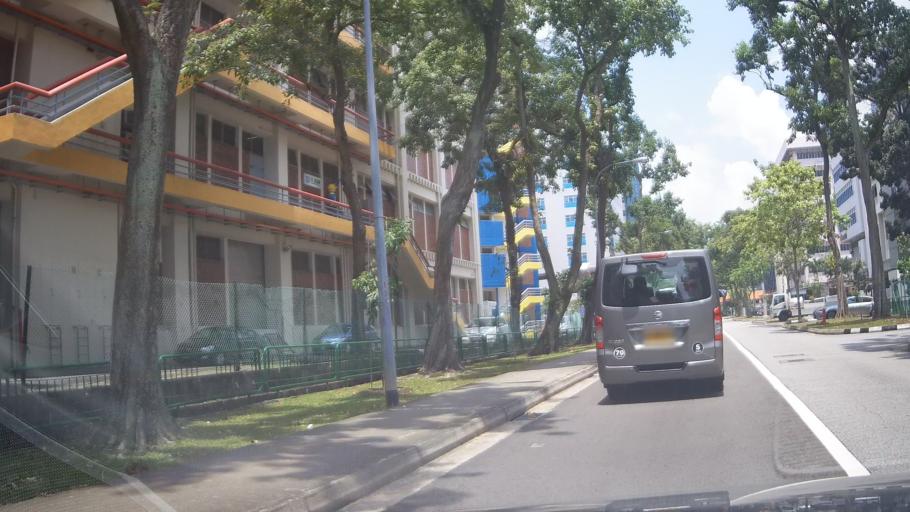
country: SG
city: Singapore
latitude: 1.3273
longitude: 103.8749
